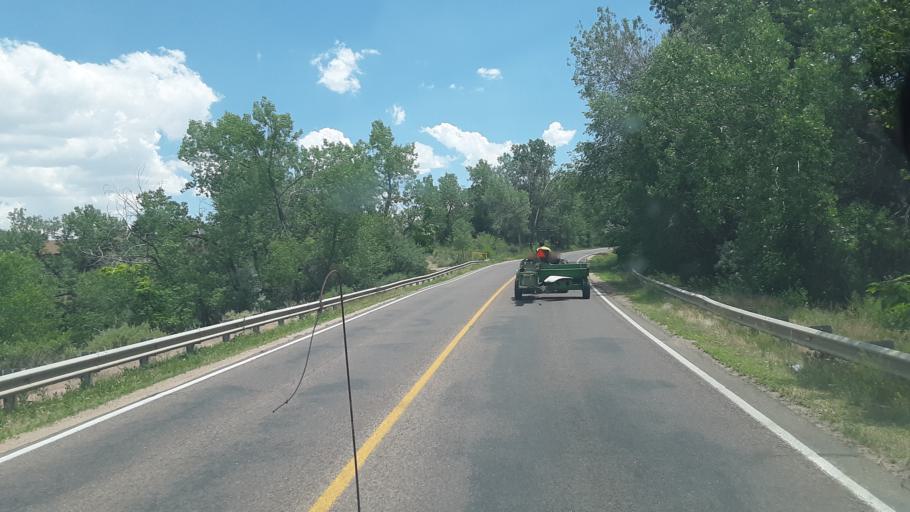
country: US
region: Colorado
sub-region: Fremont County
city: Lincoln Park
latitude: 38.4329
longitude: -105.1995
